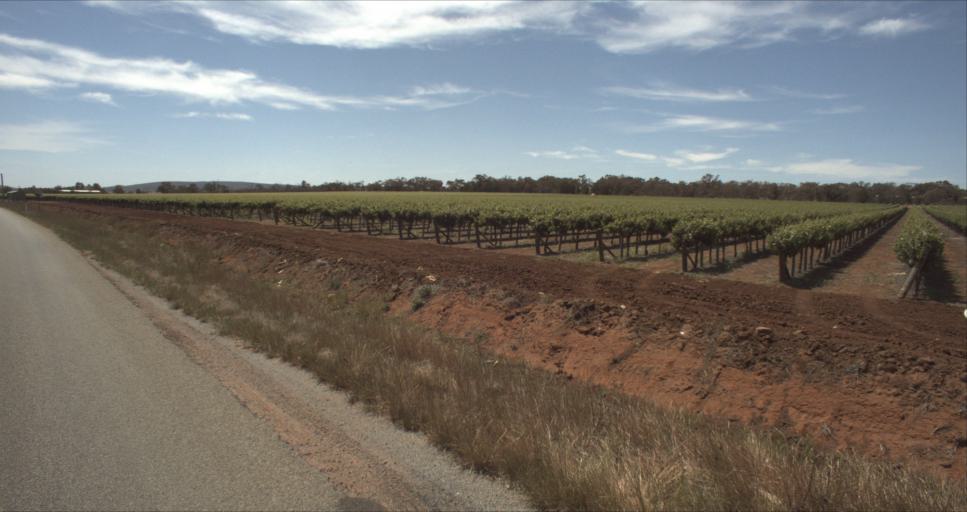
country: AU
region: New South Wales
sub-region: Leeton
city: Leeton
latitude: -34.5645
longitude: 146.4520
